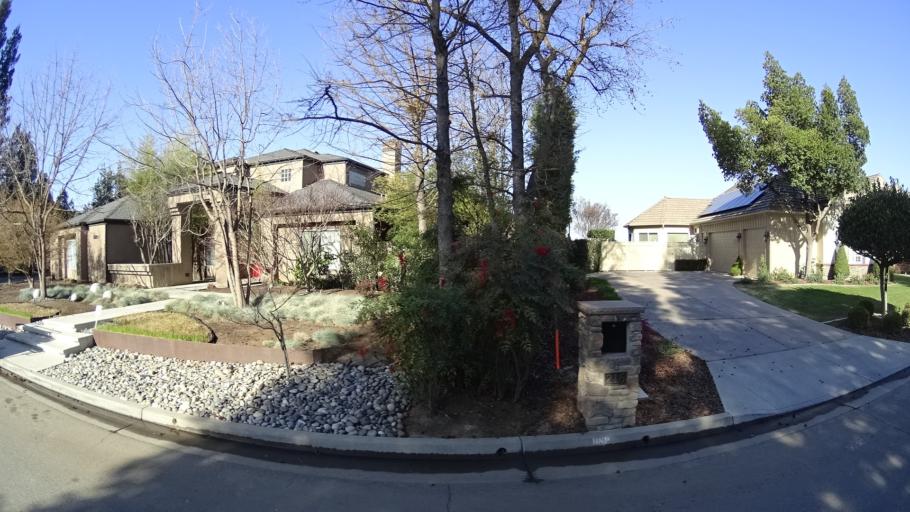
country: US
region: California
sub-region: Fresno County
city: Clovis
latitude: 36.8677
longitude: -119.7946
